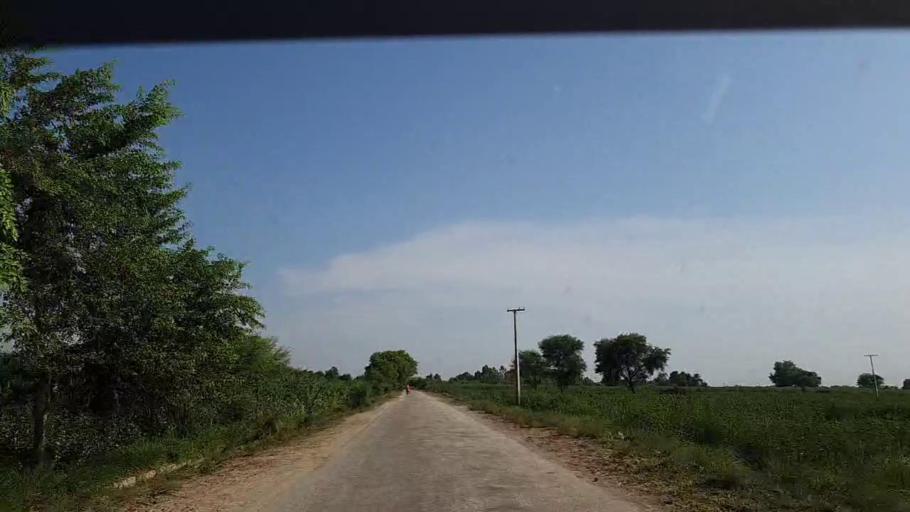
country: PK
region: Sindh
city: Adilpur
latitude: 27.9354
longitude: 69.2543
